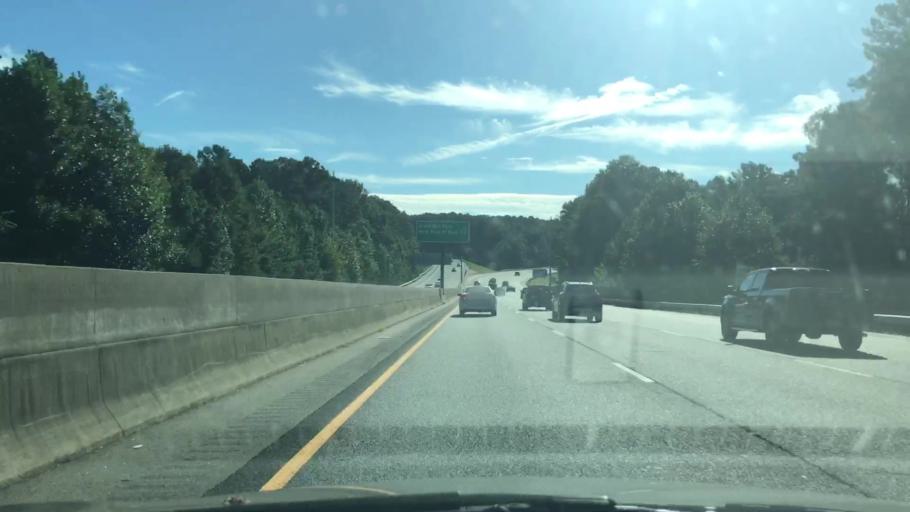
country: US
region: Georgia
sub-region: Gwinnett County
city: Mountain Park
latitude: 33.8238
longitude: -84.1428
